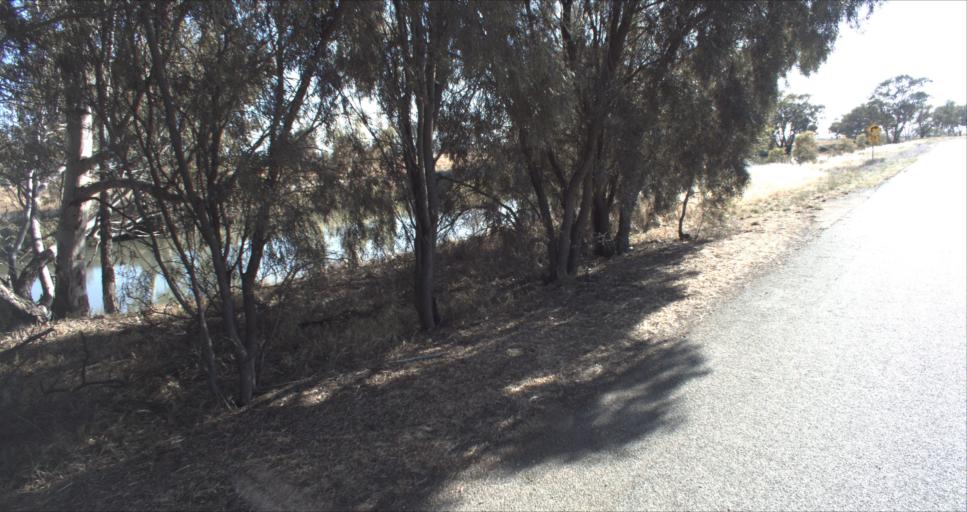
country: AU
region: New South Wales
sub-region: Leeton
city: Leeton
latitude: -34.6051
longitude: 146.2617
